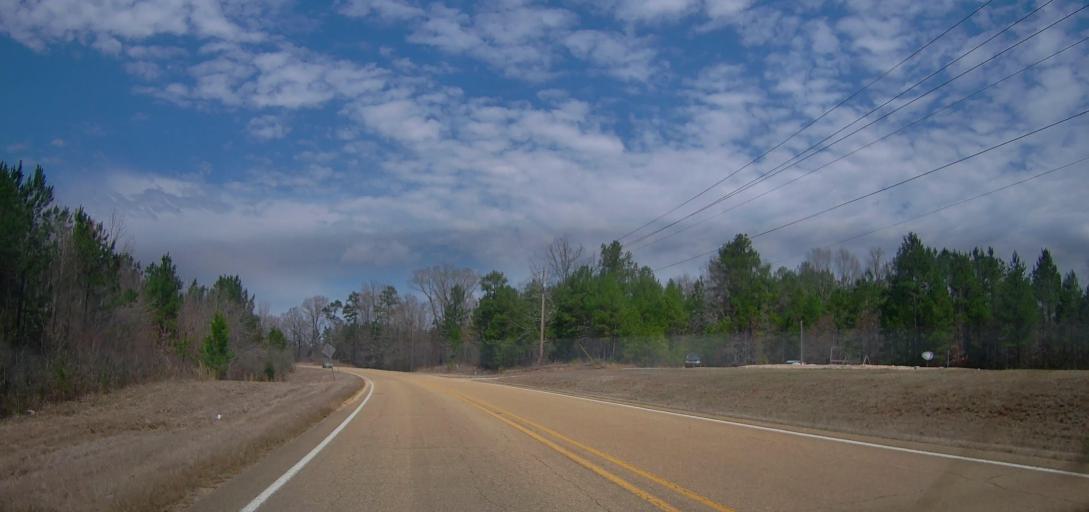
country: US
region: Mississippi
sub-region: Union County
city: New Albany
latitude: 34.6097
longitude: -89.1471
